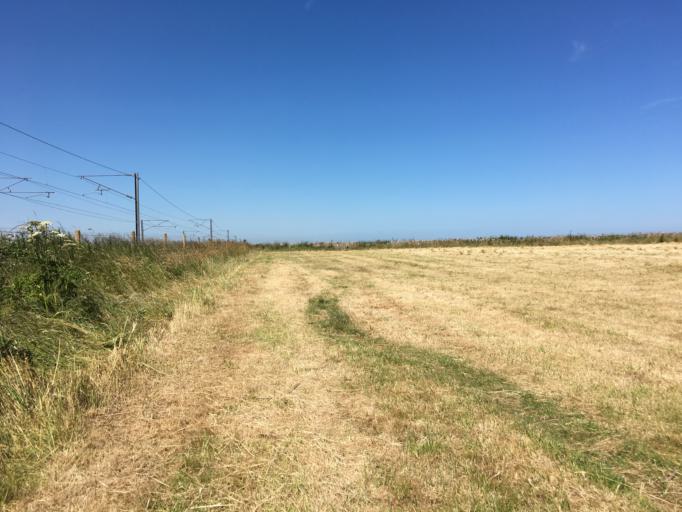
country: GB
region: England
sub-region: Northumberland
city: Ancroft
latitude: 55.7093
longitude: -1.9317
